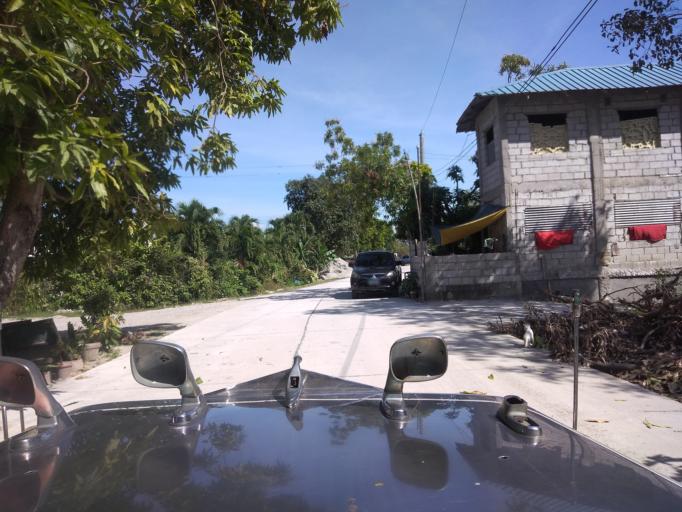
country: PH
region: Central Luzon
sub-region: Province of Pampanga
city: Magliman
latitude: 15.0269
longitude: 120.6608
